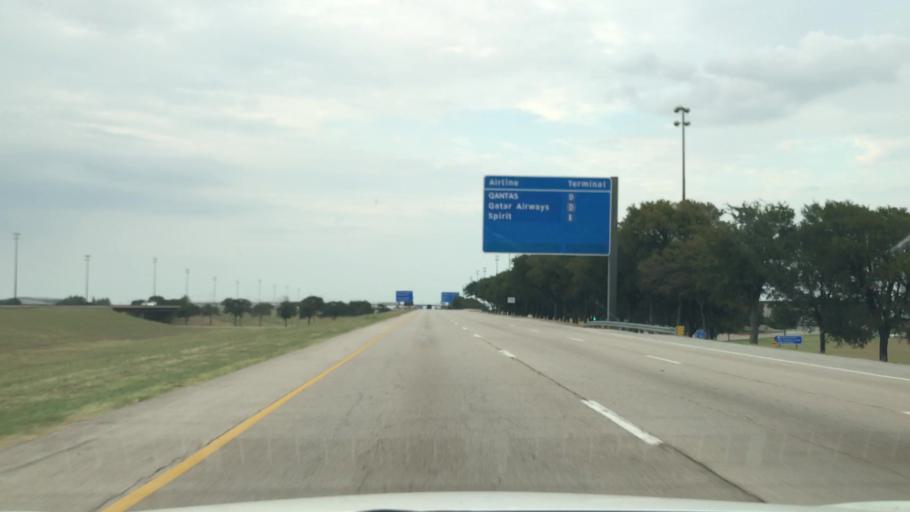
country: US
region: Texas
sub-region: Tarrant County
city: Euless
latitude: 32.8741
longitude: -97.0399
